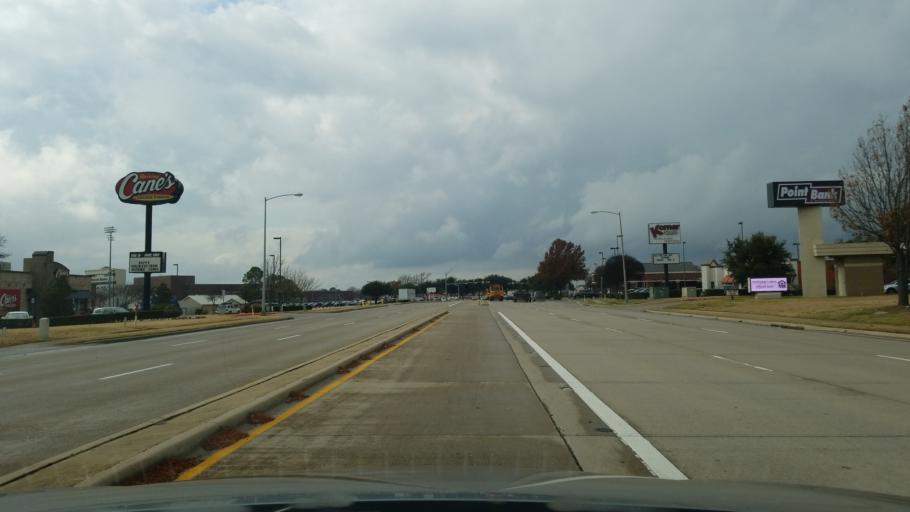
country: US
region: Texas
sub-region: Denton County
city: Lewisville
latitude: 33.0436
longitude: -97.0160
